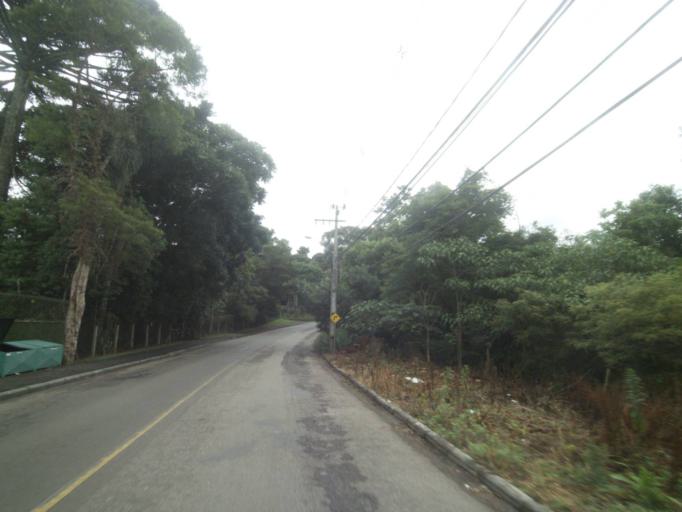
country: BR
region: Parana
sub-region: Curitiba
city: Curitiba
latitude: -25.4546
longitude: -49.3337
